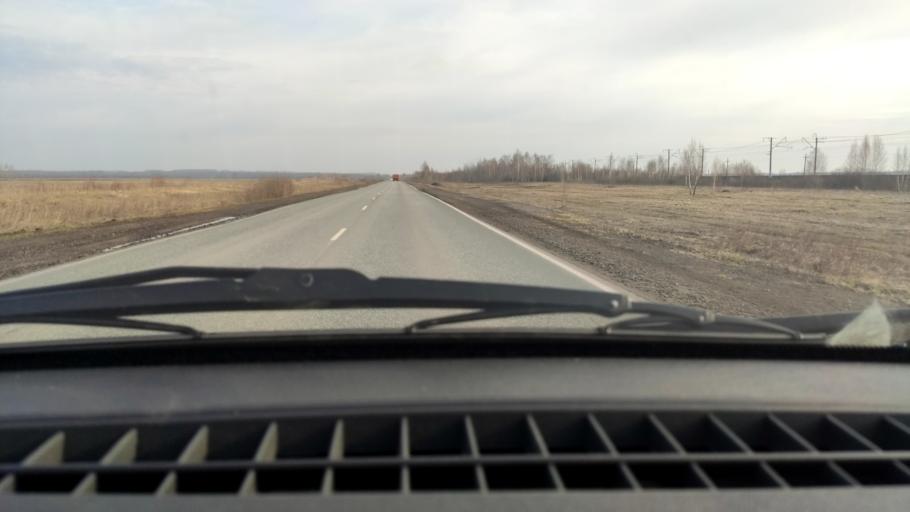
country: RU
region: Bashkortostan
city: Chishmy
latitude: 54.4217
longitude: 55.2289
